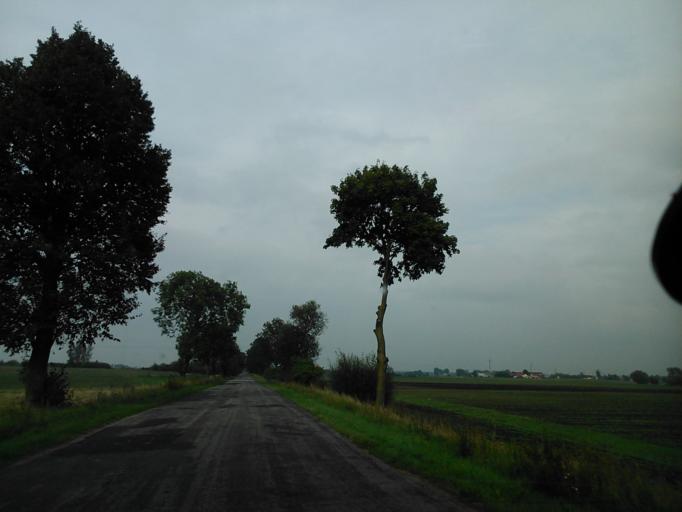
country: PL
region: Kujawsko-Pomorskie
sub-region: Powiat wabrzeski
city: Pluznica
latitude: 53.2443
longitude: 18.8204
